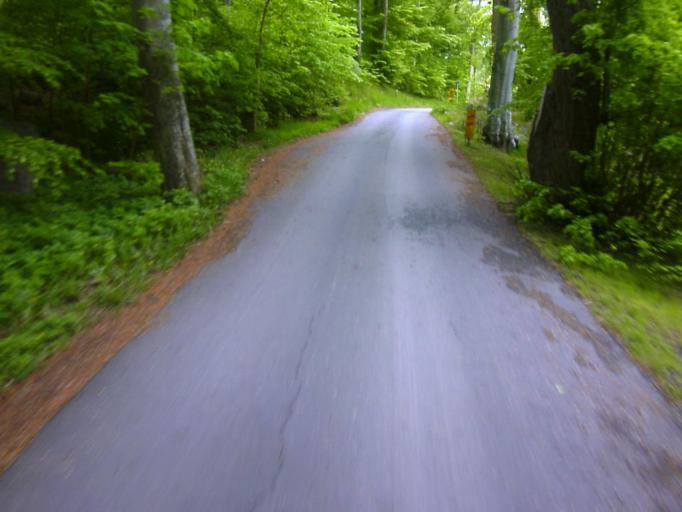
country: SE
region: Blekinge
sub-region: Solvesborgs Kommun
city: Soelvesborg
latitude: 56.0595
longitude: 14.5517
